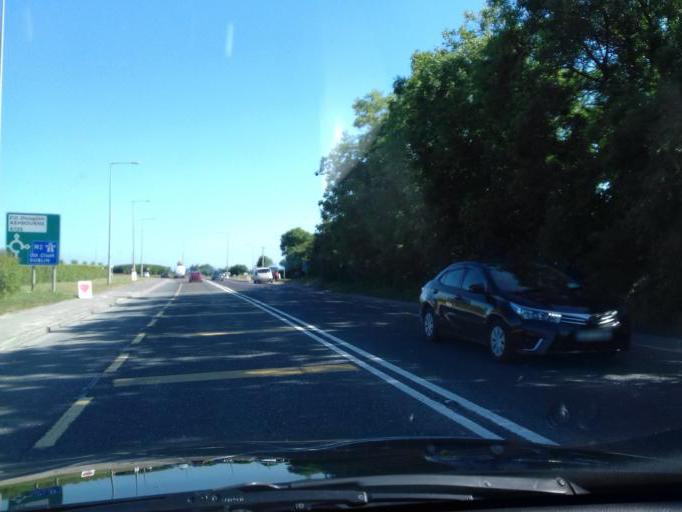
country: IE
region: Leinster
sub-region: An Mhi
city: Ashbourne
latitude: 53.5284
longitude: -6.4181
